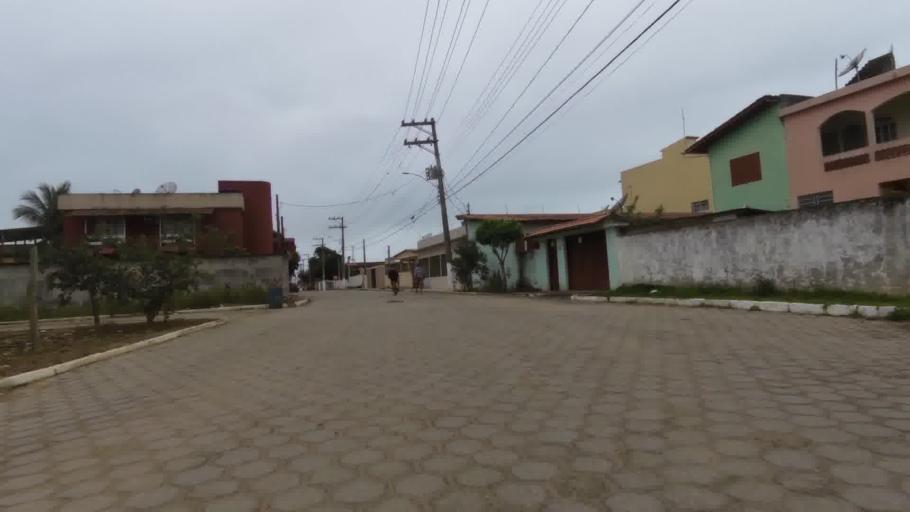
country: BR
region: Espirito Santo
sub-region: Marataizes
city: Marataizes
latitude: -21.0453
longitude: -40.8366
